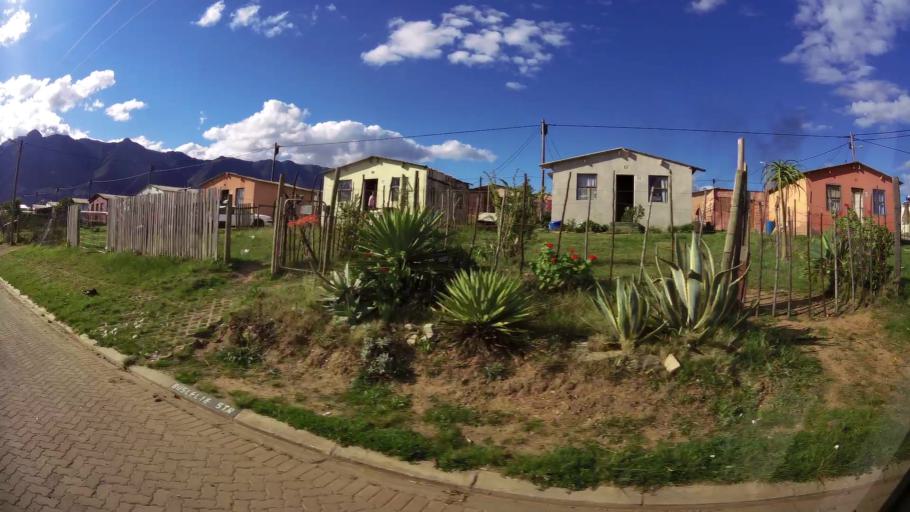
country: ZA
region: Western Cape
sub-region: Overberg District Municipality
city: Swellendam
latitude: -34.0330
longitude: 20.4510
